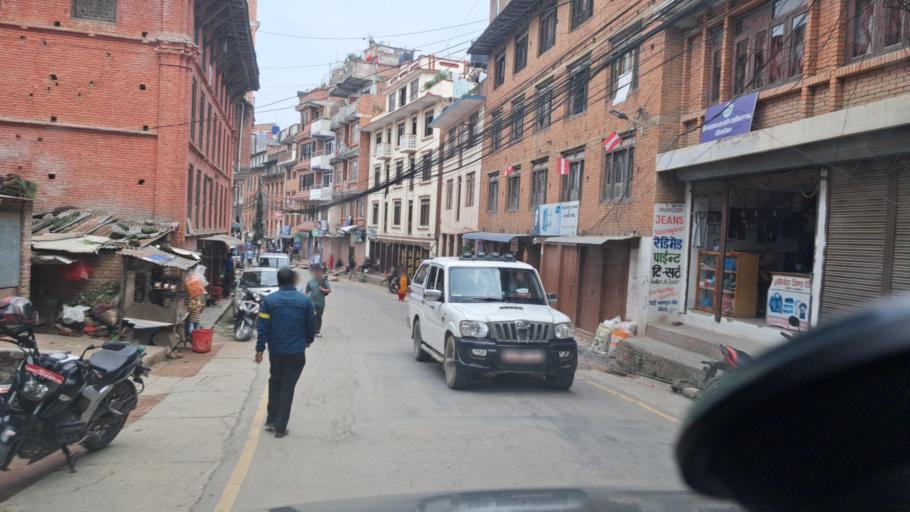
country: NP
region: Central Region
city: Banepa
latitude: 27.6174
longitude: 85.5553
